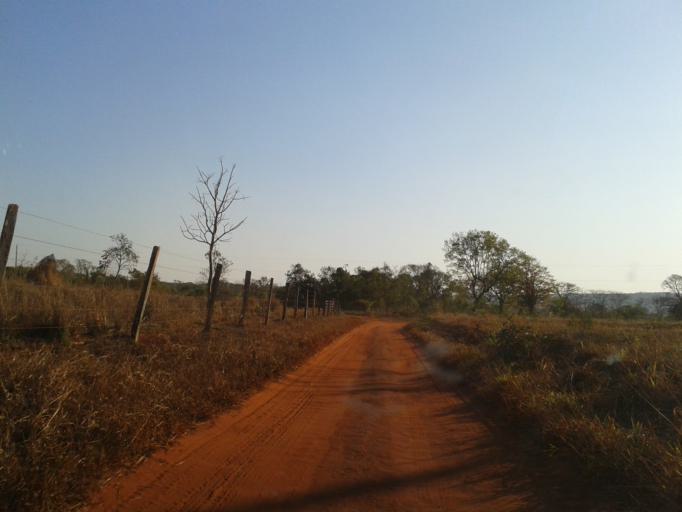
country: BR
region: Minas Gerais
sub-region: Ituiutaba
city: Ituiutaba
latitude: -19.2444
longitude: -49.5970
